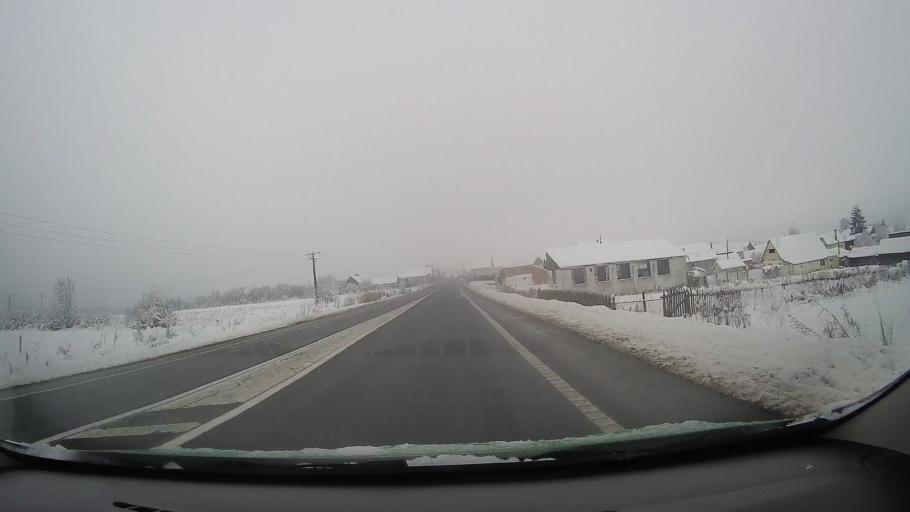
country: RO
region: Sibiu
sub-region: Oras Saliste
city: Saliste
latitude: 45.7863
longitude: 23.9331
